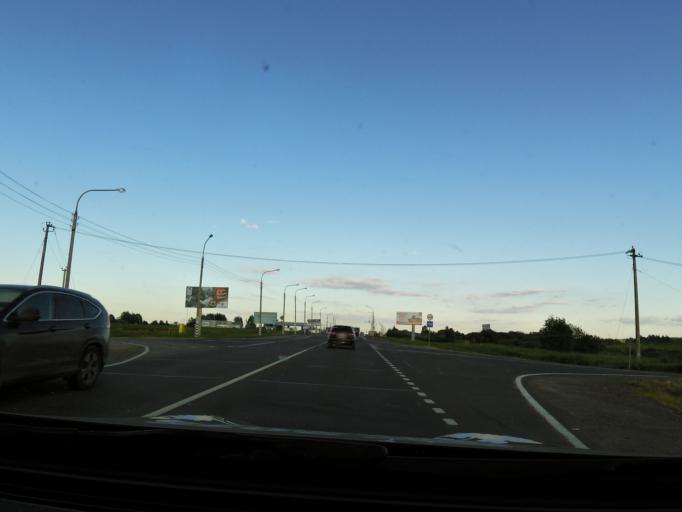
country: RU
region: Vologda
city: Vologda
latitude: 59.1739
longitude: 39.9006
